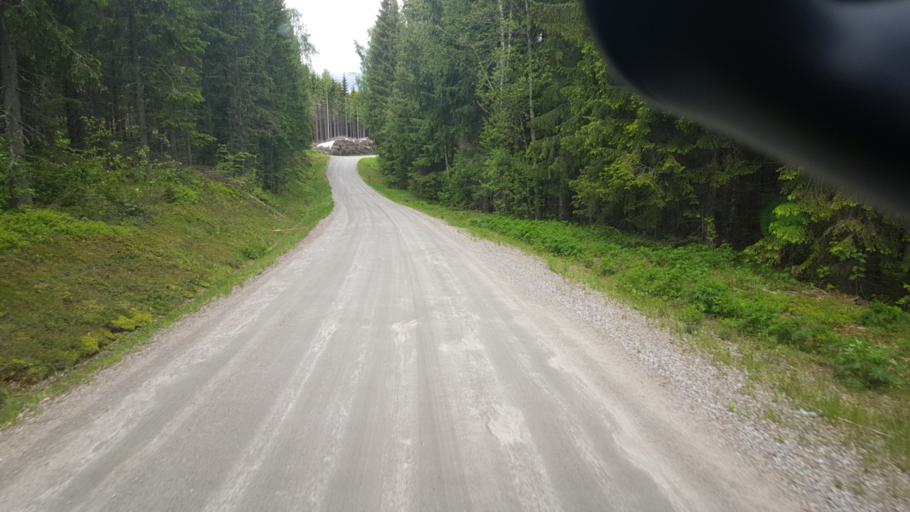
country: SE
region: Vaermland
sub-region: Eda Kommun
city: Amotfors
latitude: 59.8438
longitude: 12.5273
